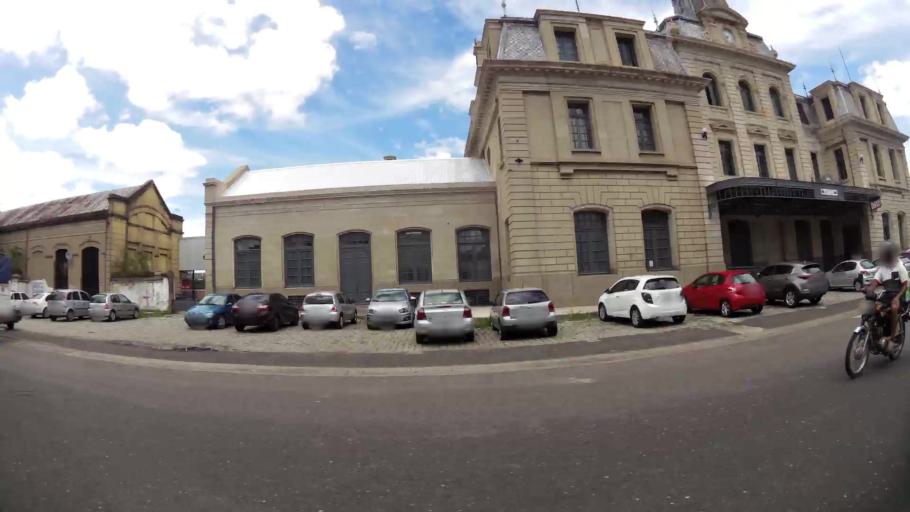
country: AR
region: Santa Fe
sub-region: Departamento de Rosario
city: Rosario
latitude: -32.9690
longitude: -60.6365
